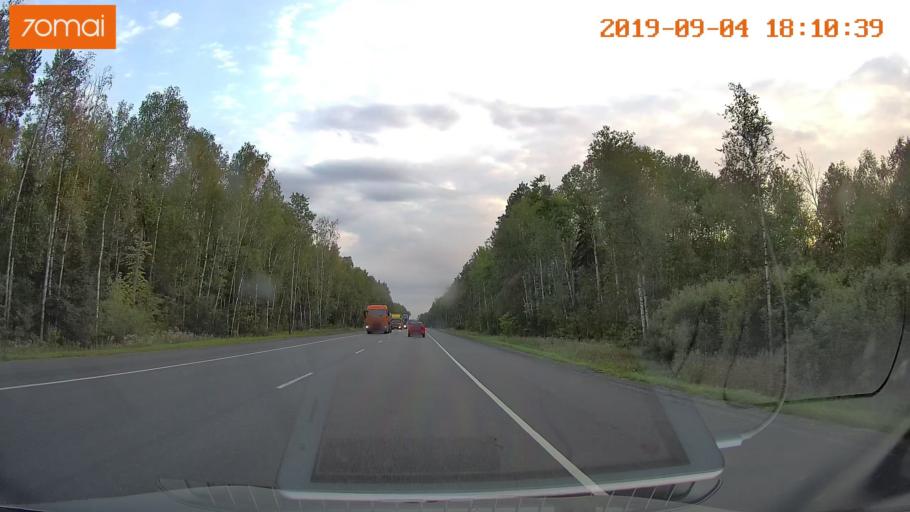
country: RU
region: Moskovskaya
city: Lopatinskiy
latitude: 55.3856
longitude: 38.7629
